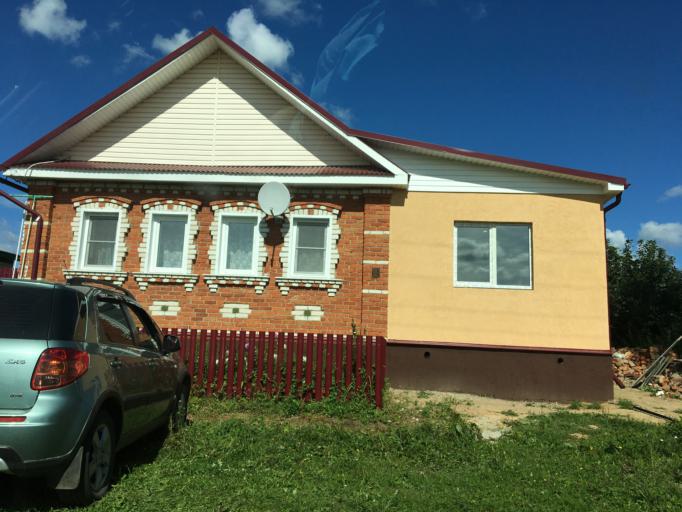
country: RU
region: Nizjnij Novgorod
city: Lyskovo
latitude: 55.9865
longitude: 45.0407
